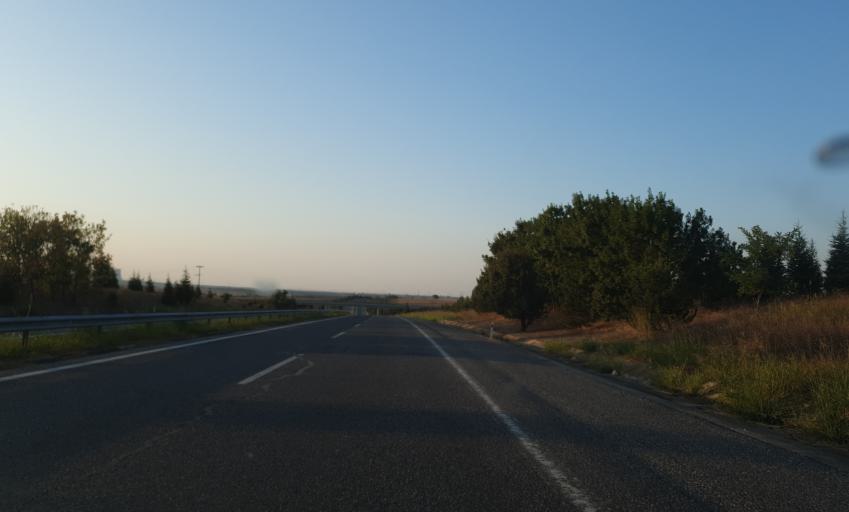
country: TR
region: Kirklareli
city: Luleburgaz
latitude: 41.4152
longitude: 27.3867
